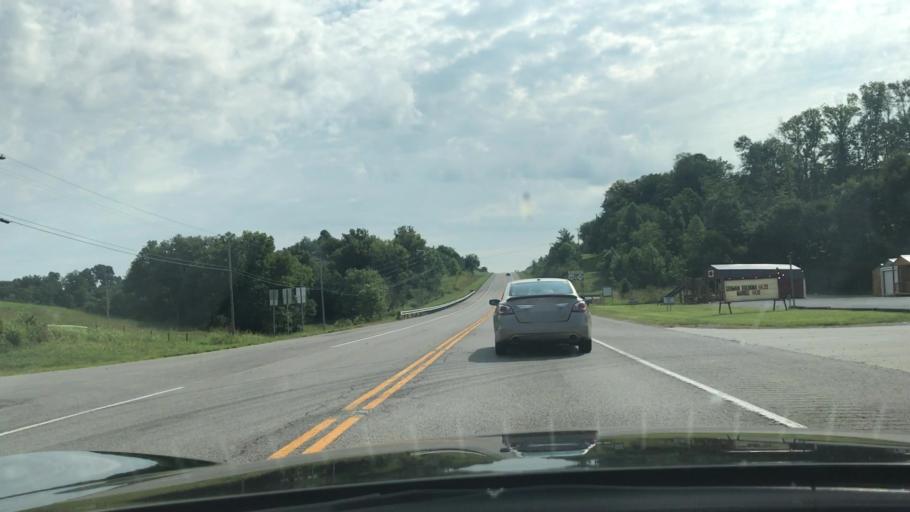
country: US
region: Kentucky
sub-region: Green County
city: Greensburg
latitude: 37.2943
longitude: -85.4667
